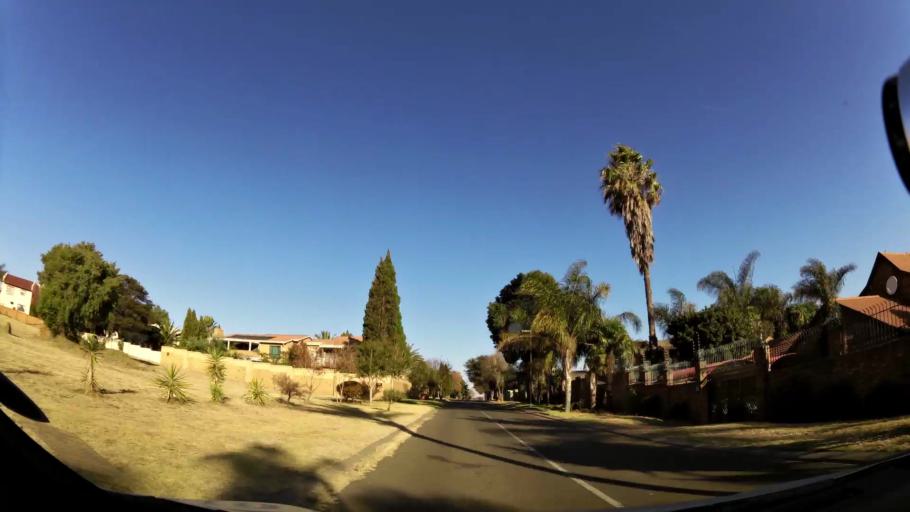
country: ZA
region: Gauteng
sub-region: City of Johannesburg Metropolitan Municipality
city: Johannesburg
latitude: -26.2842
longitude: 28.0702
